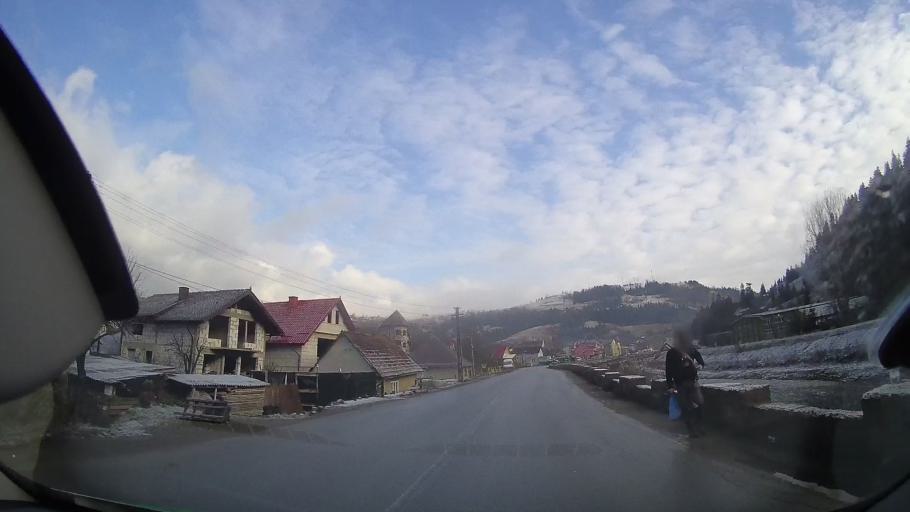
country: RO
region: Alba
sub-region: Oras Campeni
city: Campeni
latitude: 46.3597
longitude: 23.0453
